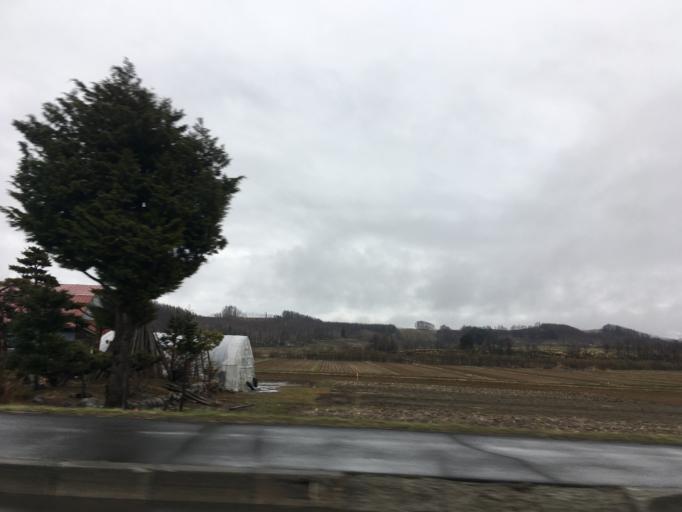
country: JP
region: Hokkaido
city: Nayoro
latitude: 44.0997
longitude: 142.4754
